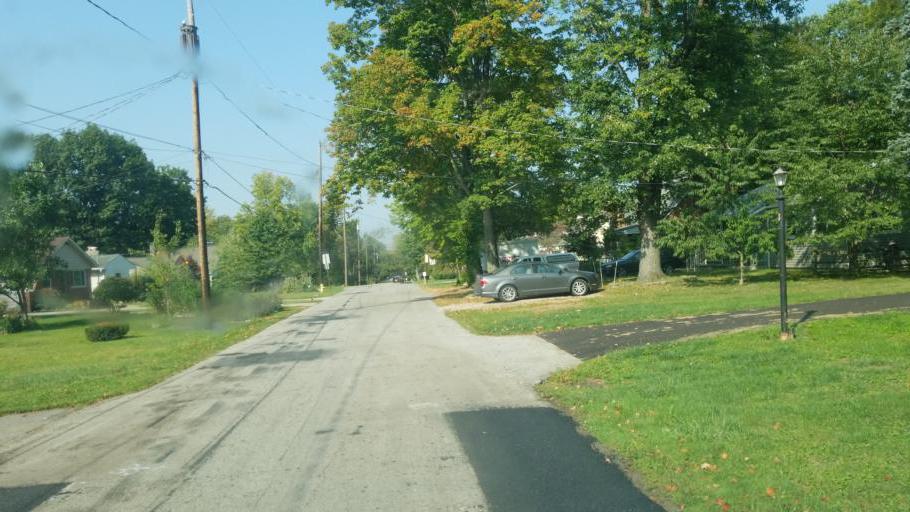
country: US
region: Ohio
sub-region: Franklin County
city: Worthington
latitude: 40.0698
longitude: -83.0232
